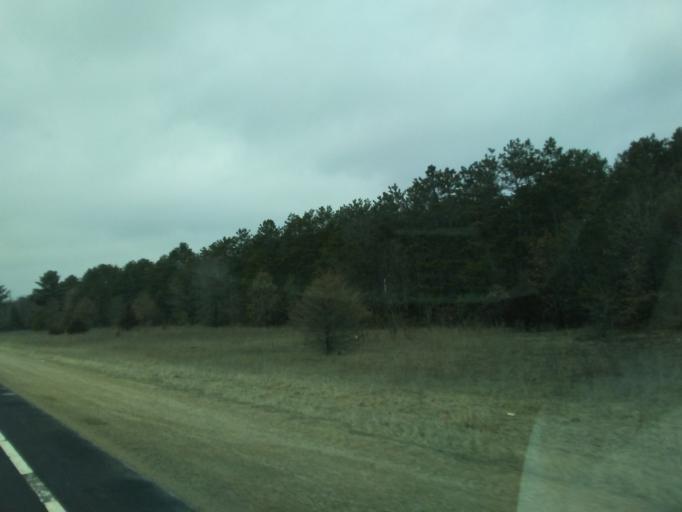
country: US
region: Wisconsin
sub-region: Sauk County
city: Spring Green
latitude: 43.1961
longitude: -90.2328
